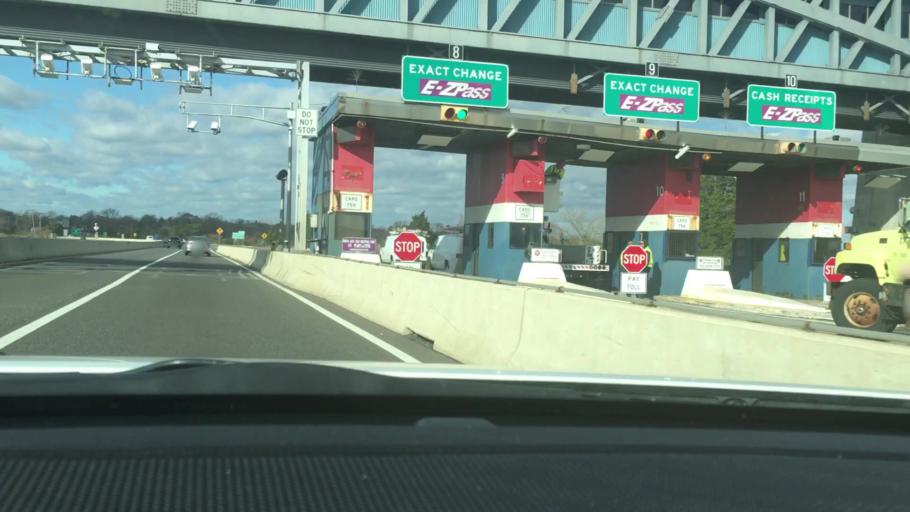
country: US
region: New Jersey
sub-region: Atlantic County
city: Pleasantville
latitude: 39.3917
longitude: -74.5102
